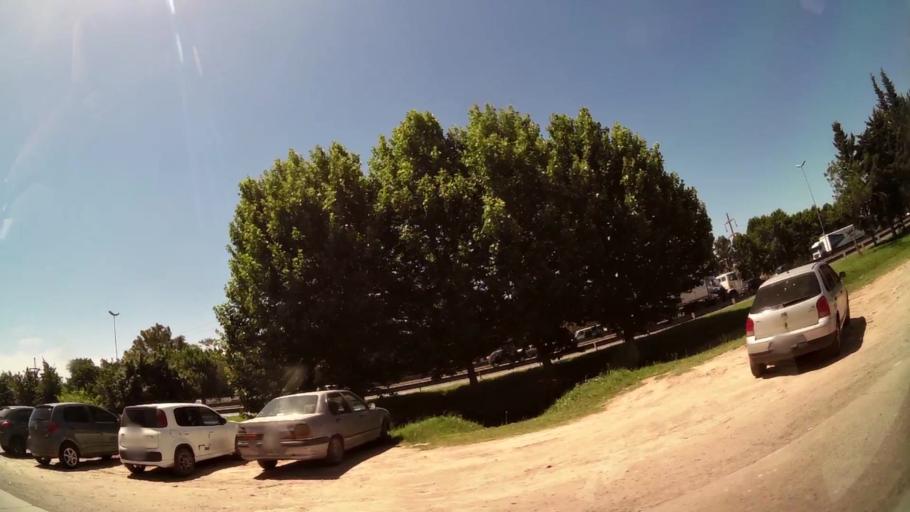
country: AR
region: Buenos Aires
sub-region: Partido de Tigre
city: Tigre
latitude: -34.4811
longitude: -58.6425
